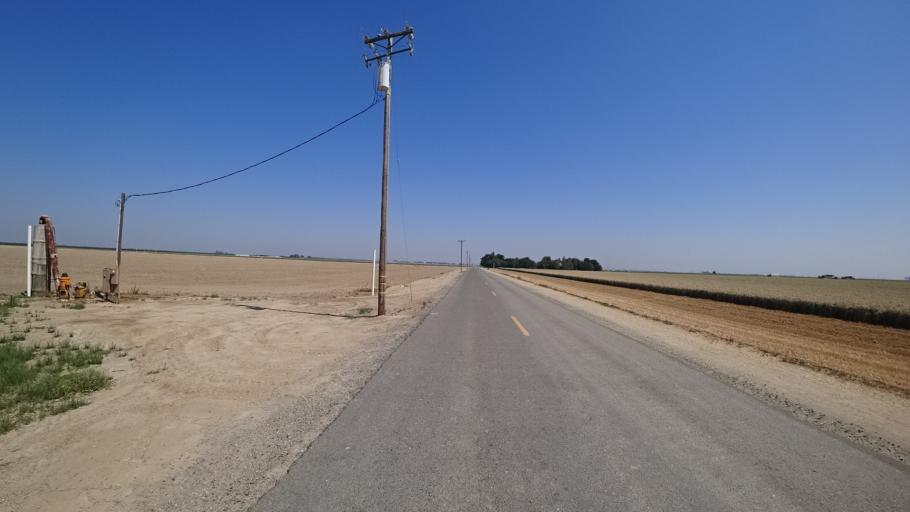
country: US
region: California
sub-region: Tulare County
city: Goshen
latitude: 36.3838
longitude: -119.5290
